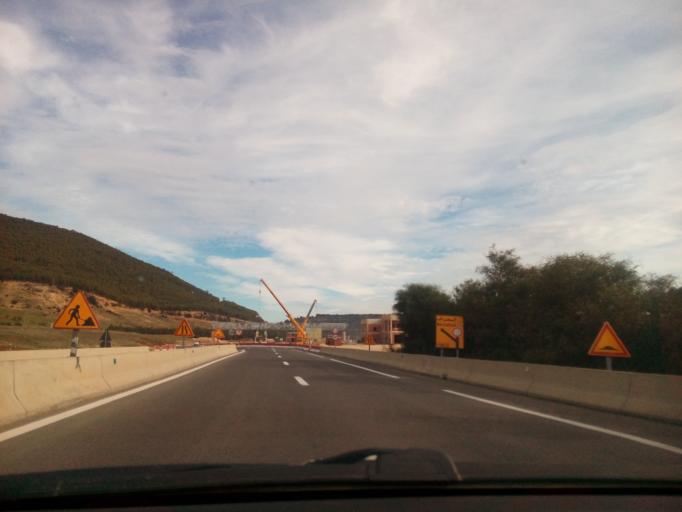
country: DZ
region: Sidi Bel Abbes
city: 'Ain el Berd
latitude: 35.3821
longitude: -0.4980
